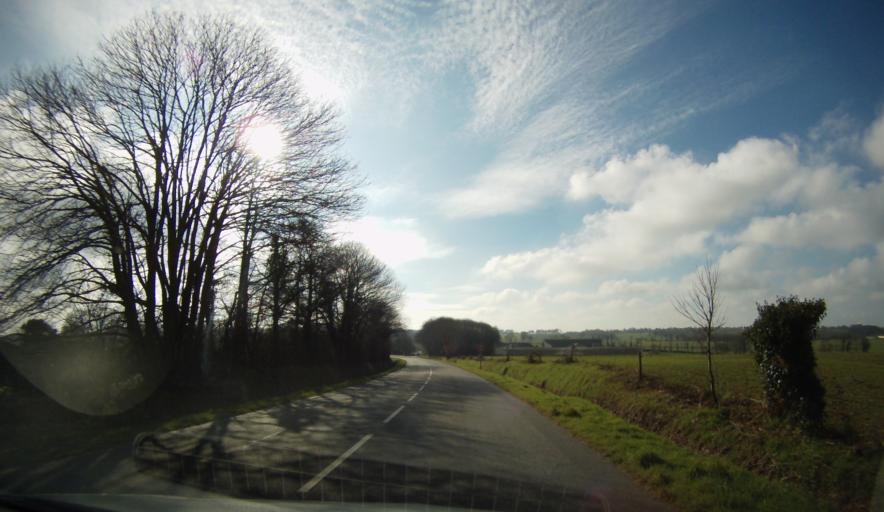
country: FR
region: Brittany
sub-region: Departement d'Ille-et-Vilaine
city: Corps-Nuds
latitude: 47.9356
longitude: -1.5591
